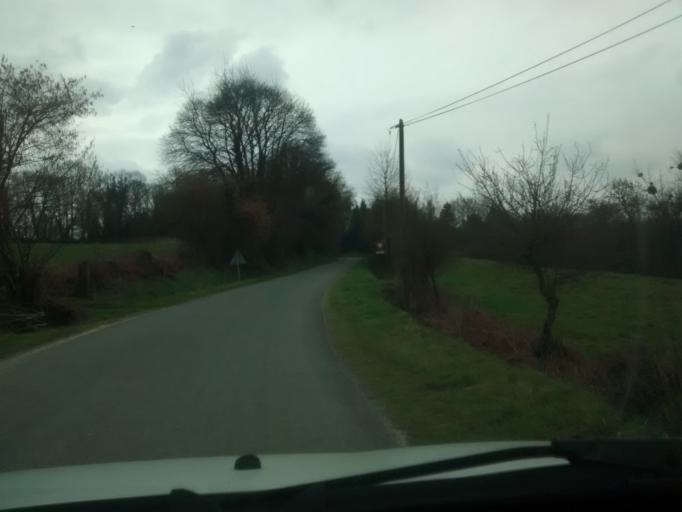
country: FR
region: Brittany
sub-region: Departement d'Ille-et-Vilaine
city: Sens-de-Bretagne
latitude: 48.3689
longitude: -1.5021
